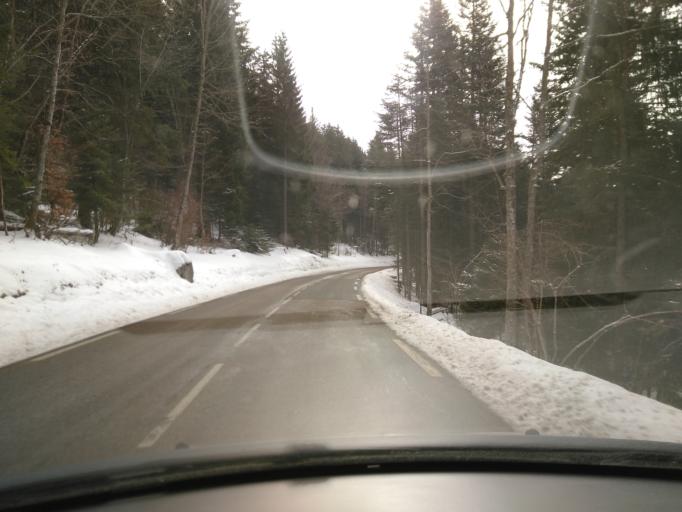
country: FR
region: Rhone-Alpes
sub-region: Departement de l'Isere
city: Le Sappey-en-Chartreuse
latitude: 45.2783
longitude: 5.7661
